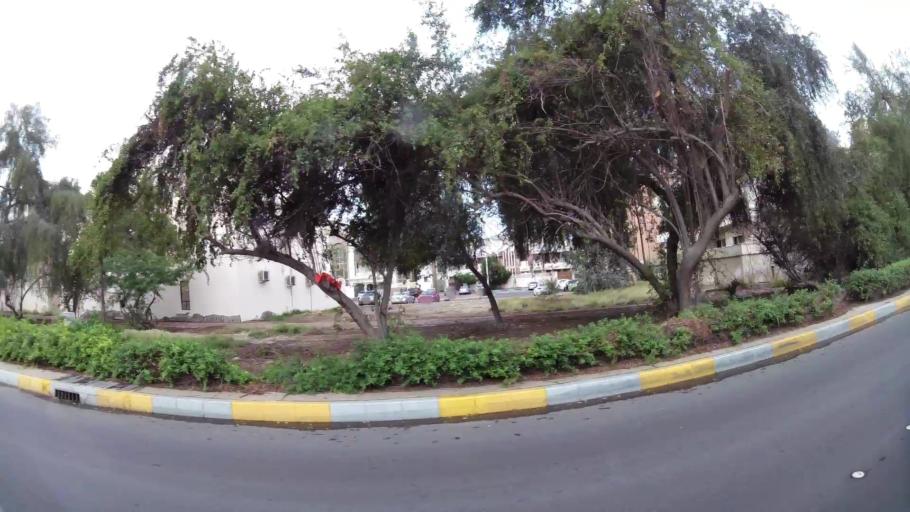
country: AE
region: Abu Dhabi
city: Abu Dhabi
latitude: 24.4425
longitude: 54.4075
